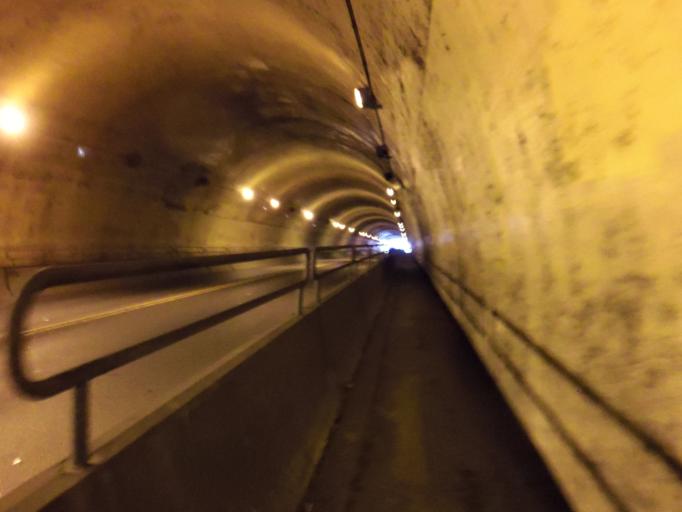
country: US
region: North Carolina
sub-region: Buncombe County
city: Asheville
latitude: 35.5986
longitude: -82.5382
